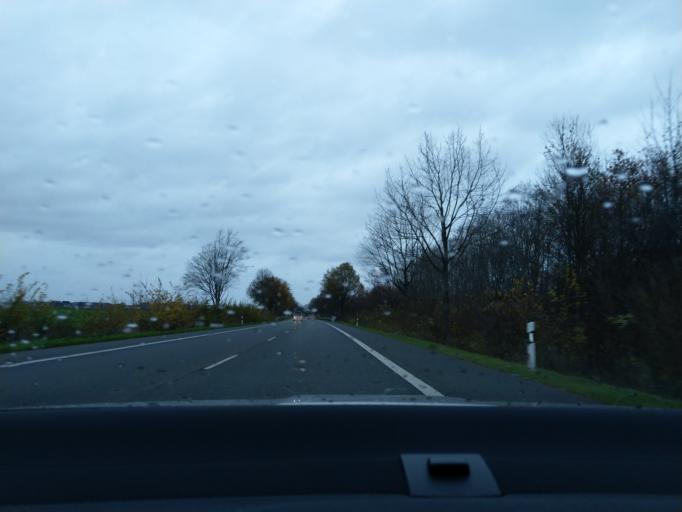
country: DE
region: North Rhine-Westphalia
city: Erkelenz
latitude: 51.0723
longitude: 6.3006
